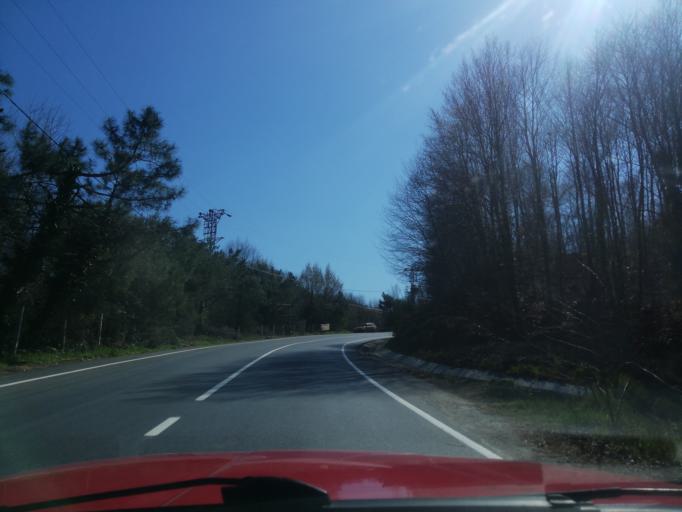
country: TR
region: Istanbul
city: Mahmut Sevket Pasa
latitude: 41.1246
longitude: 29.1562
